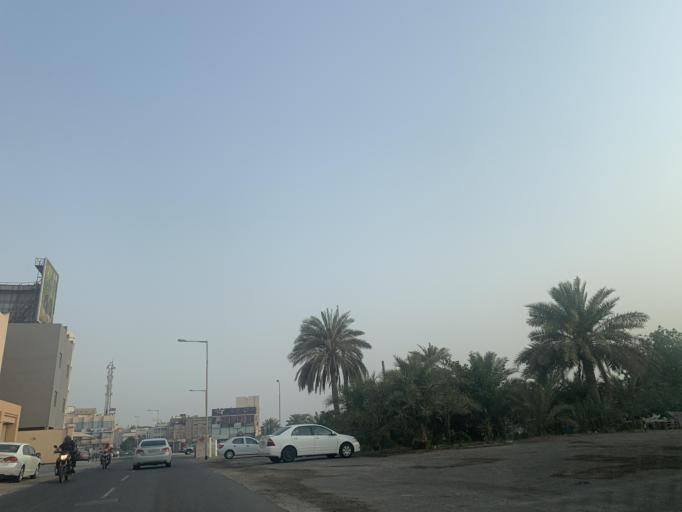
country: BH
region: Manama
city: Jidd Hafs
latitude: 26.2192
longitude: 50.5172
